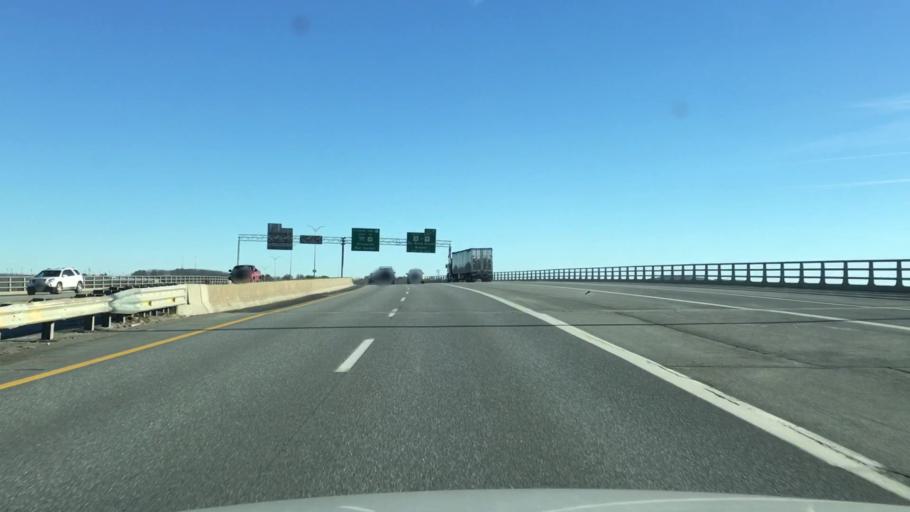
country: US
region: Maine
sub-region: Penobscot County
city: Bangor
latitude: 44.7849
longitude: -68.7779
